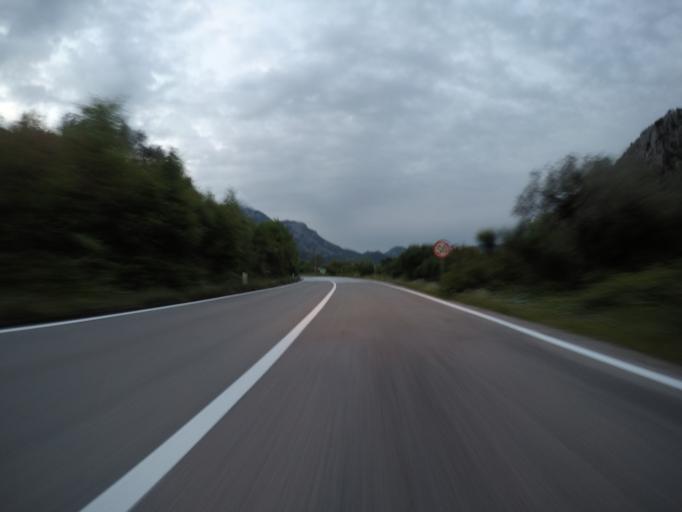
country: ME
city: Petrovac na Moru
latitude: 42.2022
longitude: 18.9602
